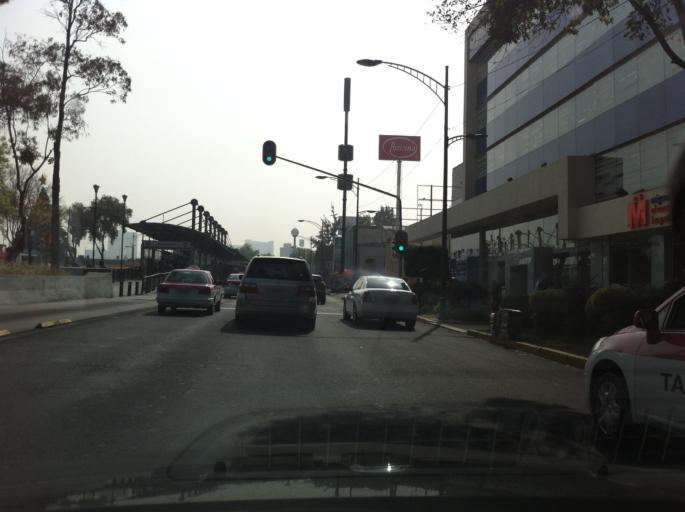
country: MX
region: Mexico City
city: Cuauhtemoc
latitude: 19.4478
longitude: -99.1529
